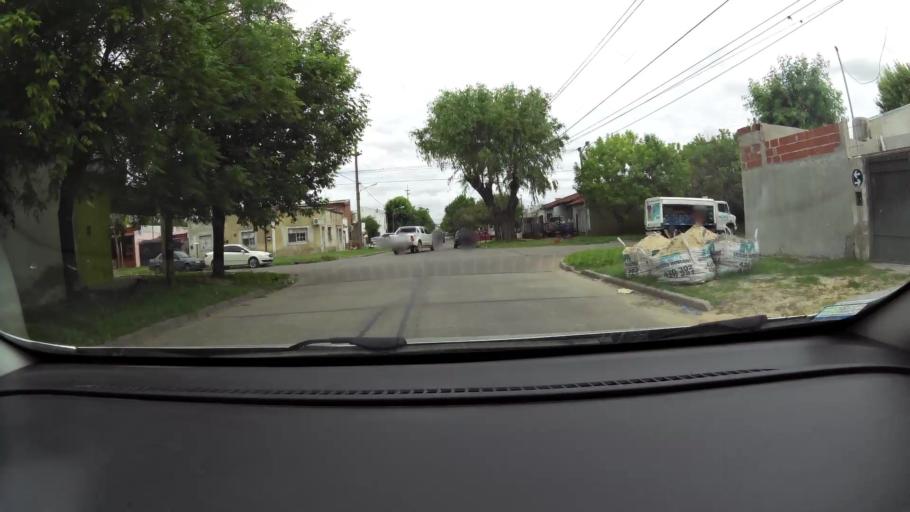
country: AR
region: Buenos Aires
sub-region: Partido de Campana
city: Campana
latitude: -34.1680
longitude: -58.9710
